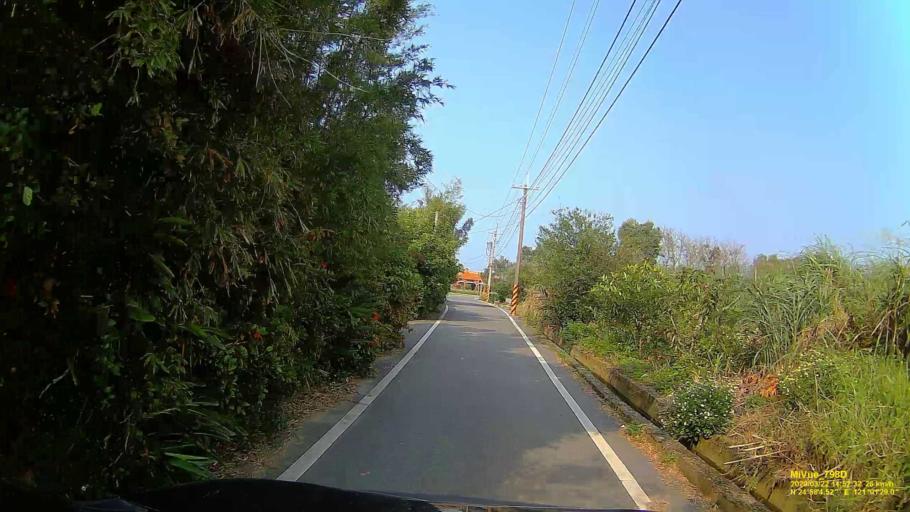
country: TW
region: Taiwan
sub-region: Hsinchu
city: Zhubei
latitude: 24.9681
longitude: 121.0248
